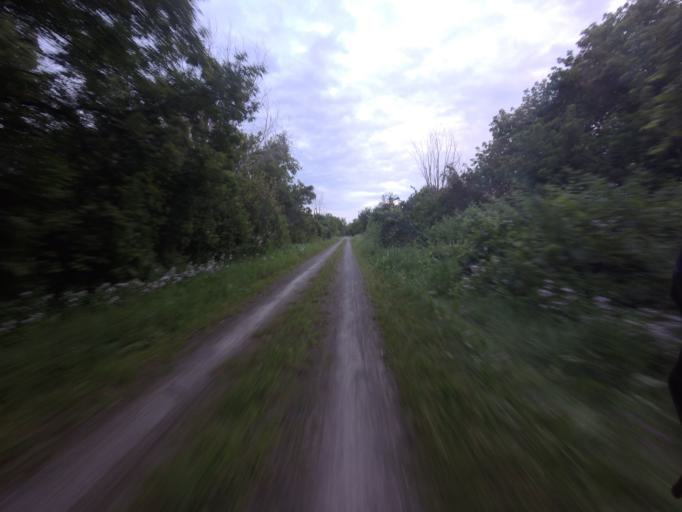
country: CA
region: Ontario
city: Carleton Place
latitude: 45.1630
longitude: -76.0746
